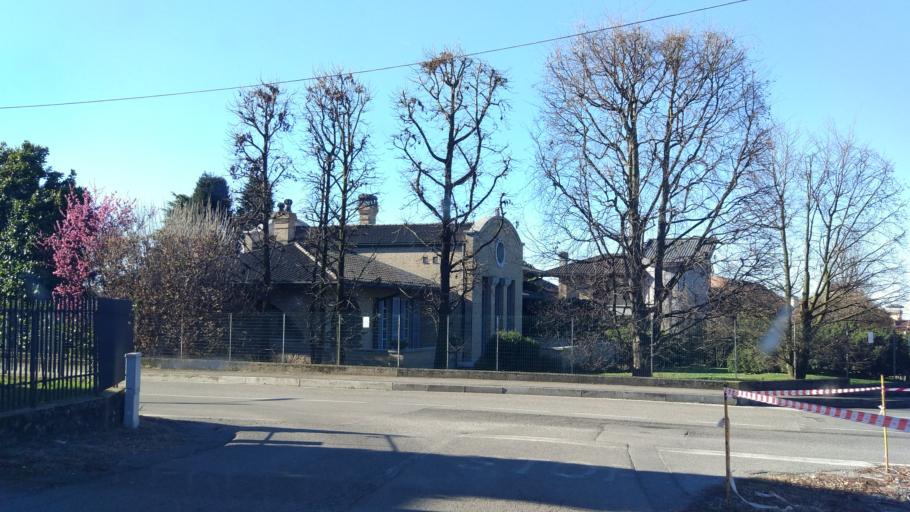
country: IT
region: Lombardy
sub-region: Provincia di Monza e Brianza
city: Giussano
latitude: 45.7033
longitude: 9.2133
